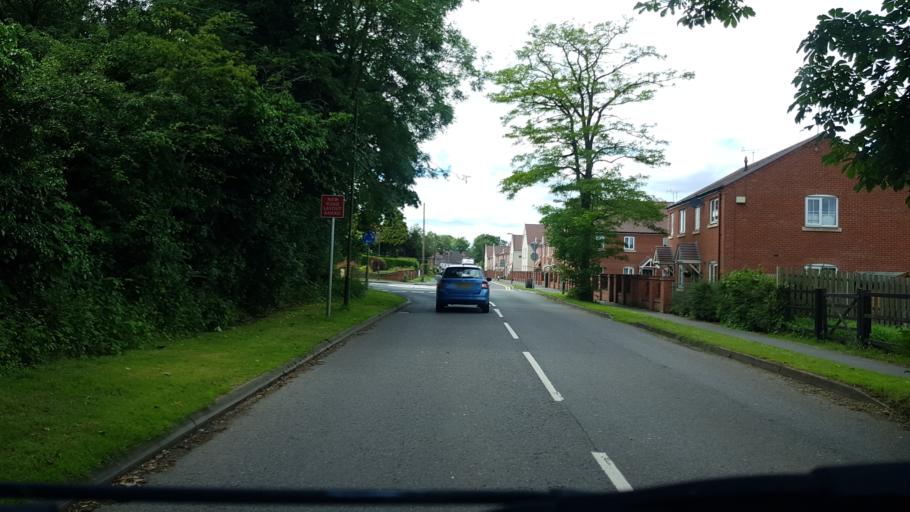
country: GB
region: England
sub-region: Worcestershire
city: Droitwich
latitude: 52.2680
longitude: -2.1390
